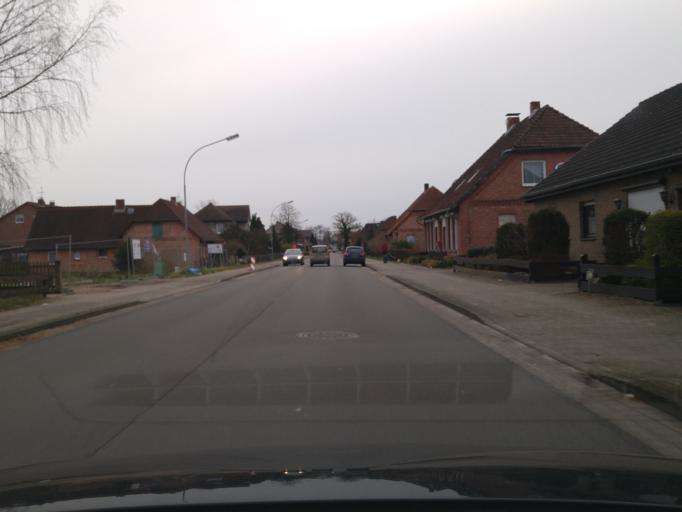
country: DE
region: Lower Saxony
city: Winsen (Aller)
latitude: 52.6891
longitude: 9.9114
